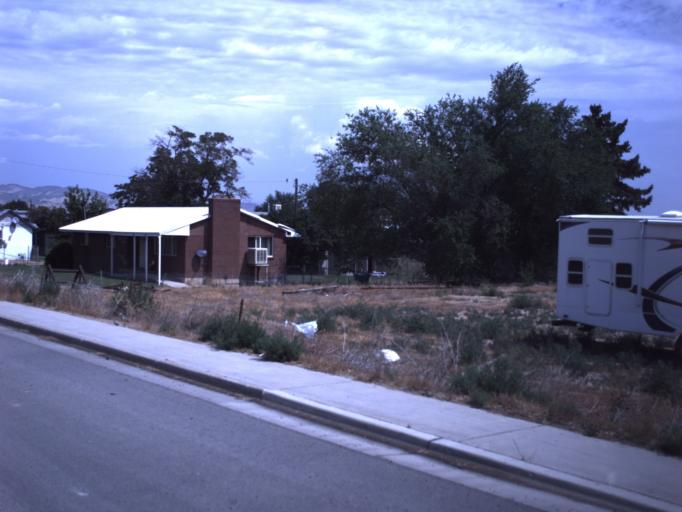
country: US
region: Utah
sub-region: Uintah County
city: Naples
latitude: 40.4247
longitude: -109.4993
